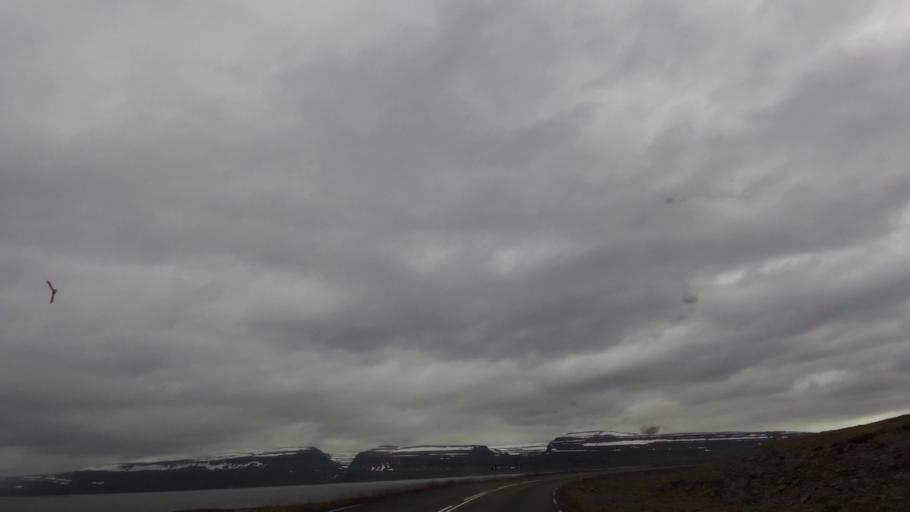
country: IS
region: Westfjords
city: Isafjoerdur
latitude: 66.0534
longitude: -22.7647
